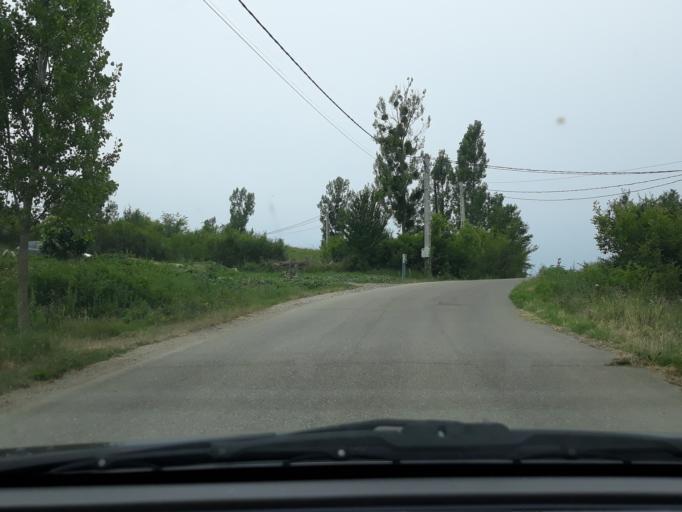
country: RO
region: Salaj
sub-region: Comuna Criseni
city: Criseni
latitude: 47.2484
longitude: 23.0709
